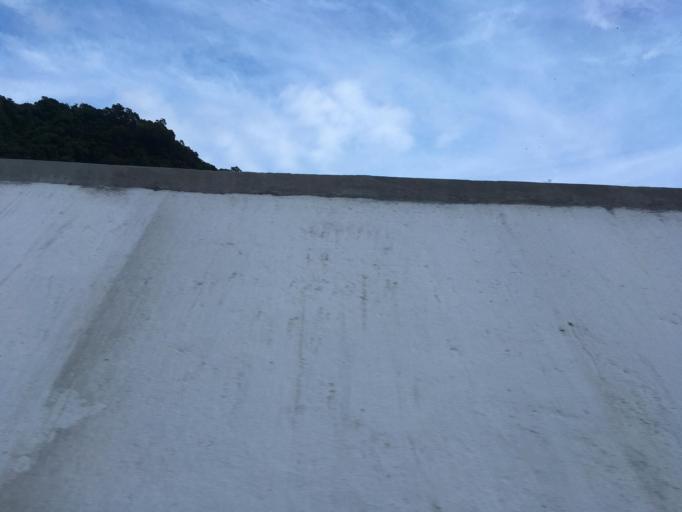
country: TW
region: Taiwan
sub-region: Yilan
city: Yilan
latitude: 24.4480
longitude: 121.7791
